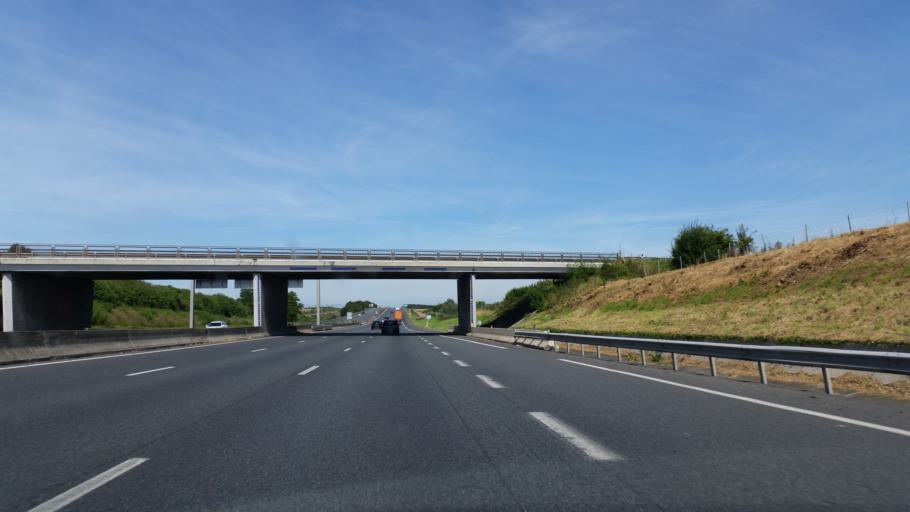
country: FR
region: Nord-Pas-de-Calais
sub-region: Departement du Pas-de-Calais
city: Bapaume
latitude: 50.1060
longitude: 2.8717
